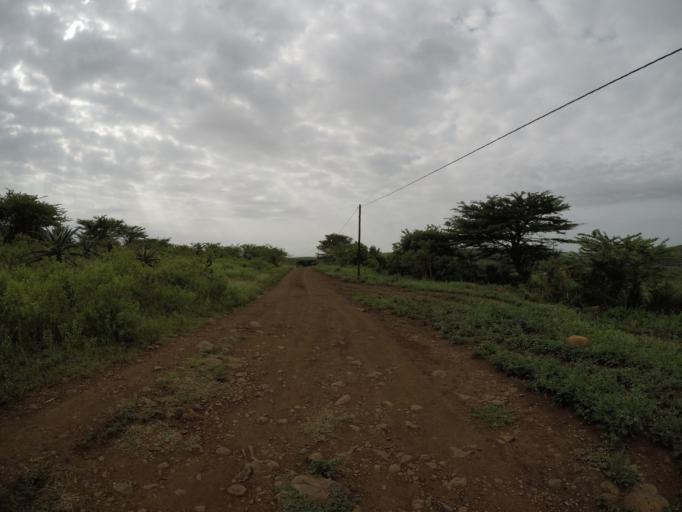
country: ZA
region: KwaZulu-Natal
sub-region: uThungulu District Municipality
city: Empangeni
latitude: -28.6406
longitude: 31.9057
